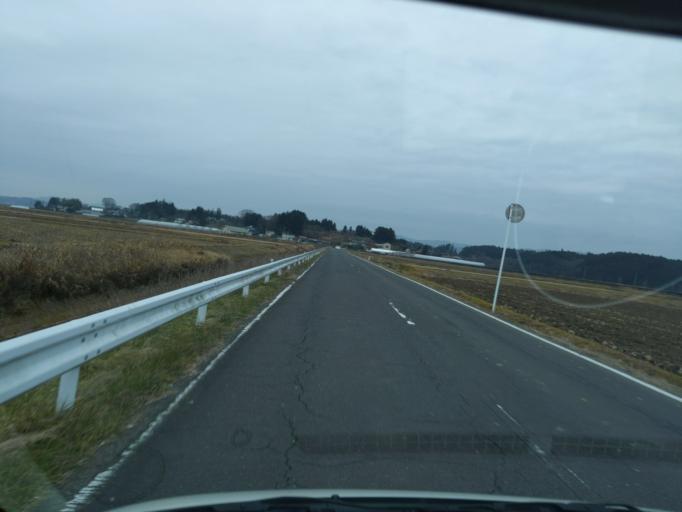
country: JP
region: Iwate
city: Ichinoseki
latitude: 38.7311
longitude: 141.2466
